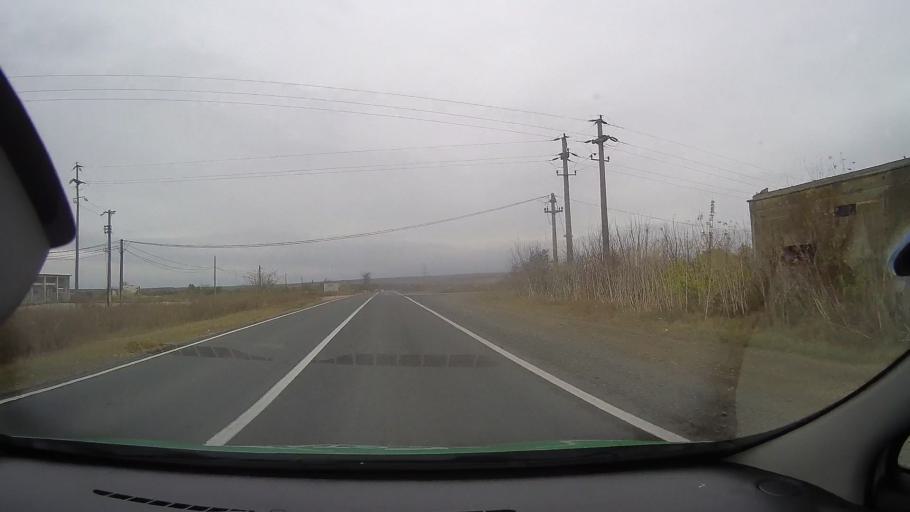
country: RO
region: Constanta
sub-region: Comuna Nicolae Balcescu
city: Dorobantu
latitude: 44.4218
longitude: 28.3116
